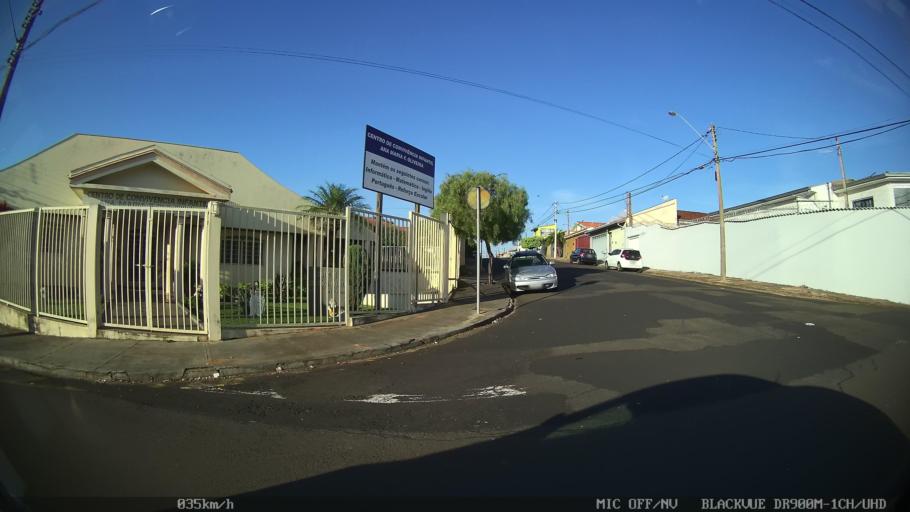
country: BR
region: Sao Paulo
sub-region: Franca
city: Franca
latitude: -20.5221
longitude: -47.3781
